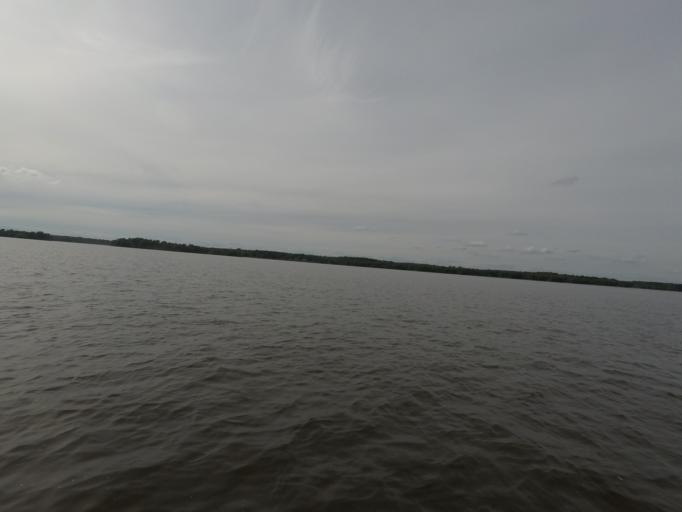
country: SE
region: Soedermanland
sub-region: Eskilstuna Kommun
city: Torshalla
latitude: 59.4742
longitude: 16.4733
